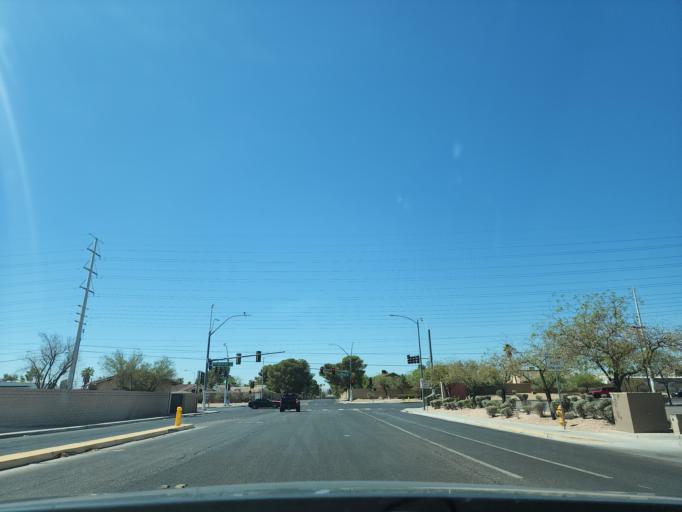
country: US
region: Nevada
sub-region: Clark County
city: Spring Valley
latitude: 36.1153
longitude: -115.2521
